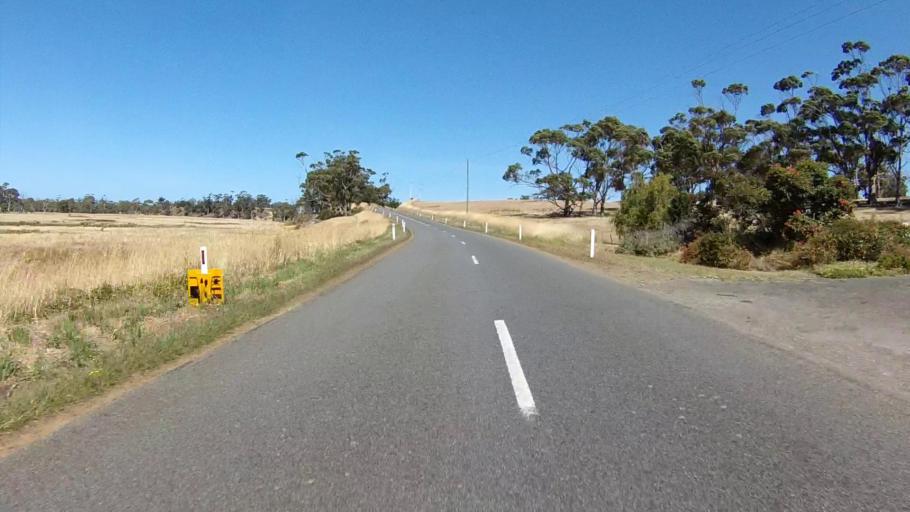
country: AU
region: Tasmania
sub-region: Sorell
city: Sorell
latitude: -42.2648
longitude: 148.0025
